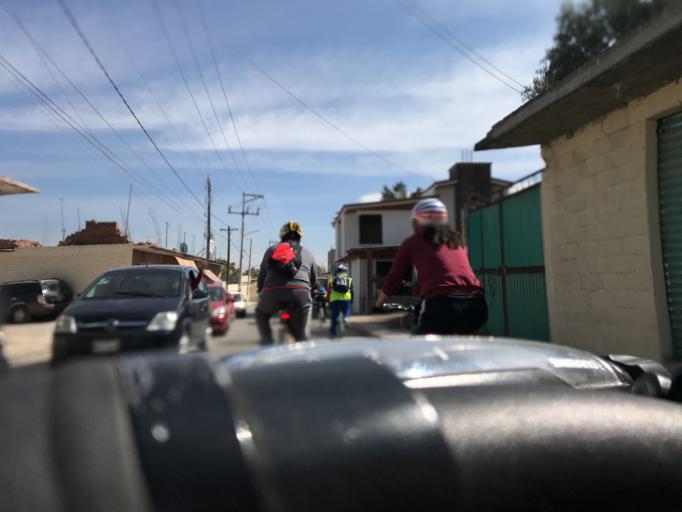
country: MX
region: Morelos
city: San Pablo Tecalco
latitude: 19.6736
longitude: -98.9600
